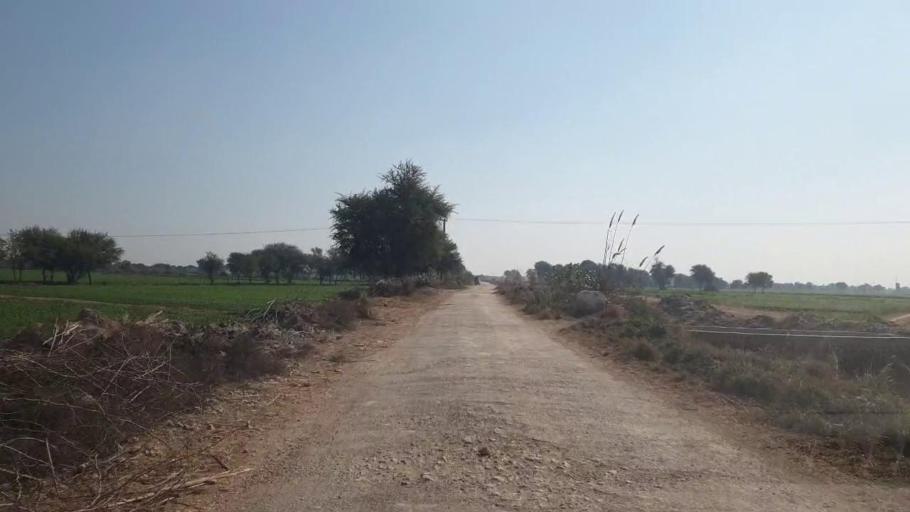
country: PK
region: Sindh
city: Shahdadpur
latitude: 25.9581
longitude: 68.6252
